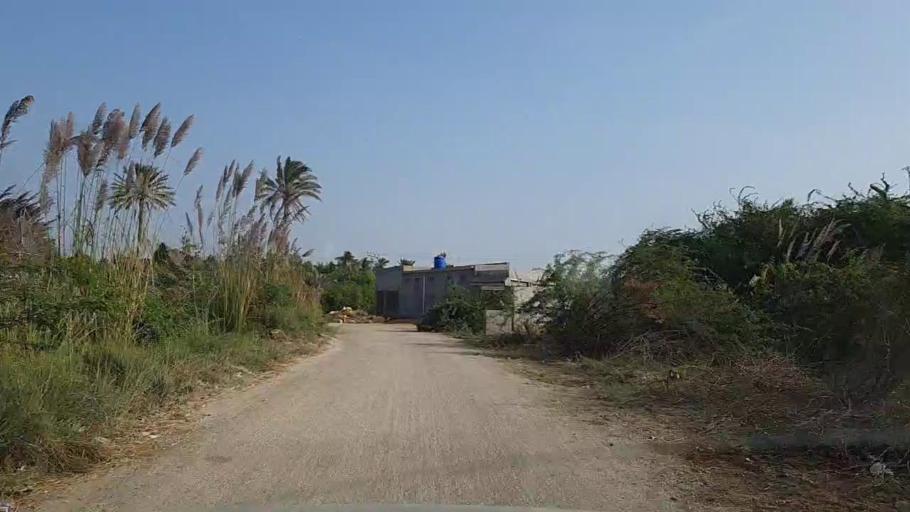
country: PK
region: Sindh
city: Mirpur Sakro
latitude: 24.5932
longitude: 67.6072
